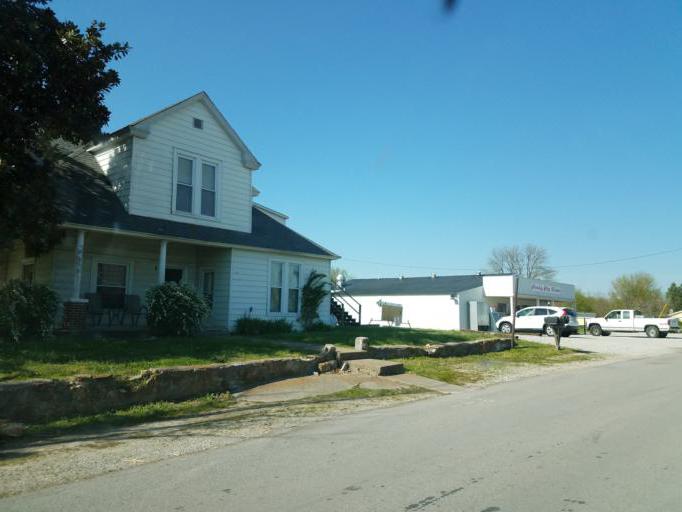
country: US
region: Kentucky
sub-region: Edmonson County
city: Brownsville
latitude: 37.1328
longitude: -86.1700
